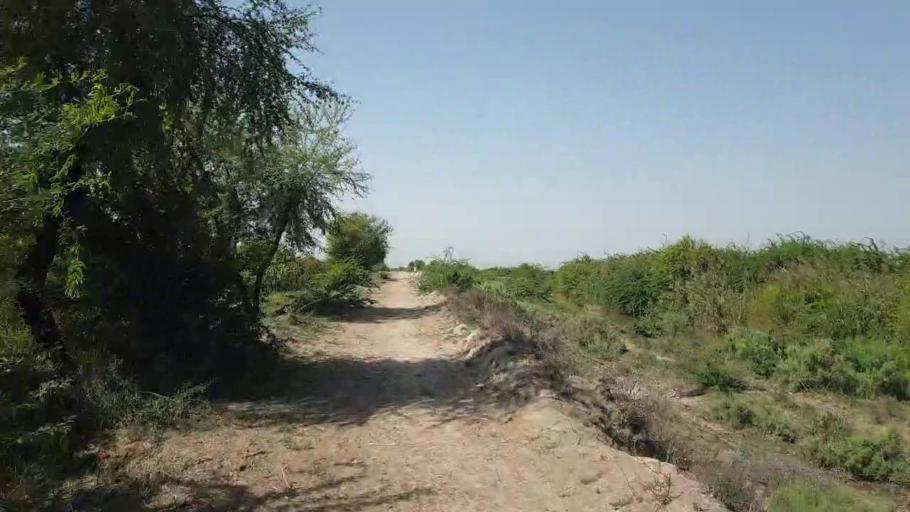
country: PK
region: Sindh
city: Tando Bago
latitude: 24.7451
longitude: 69.0284
